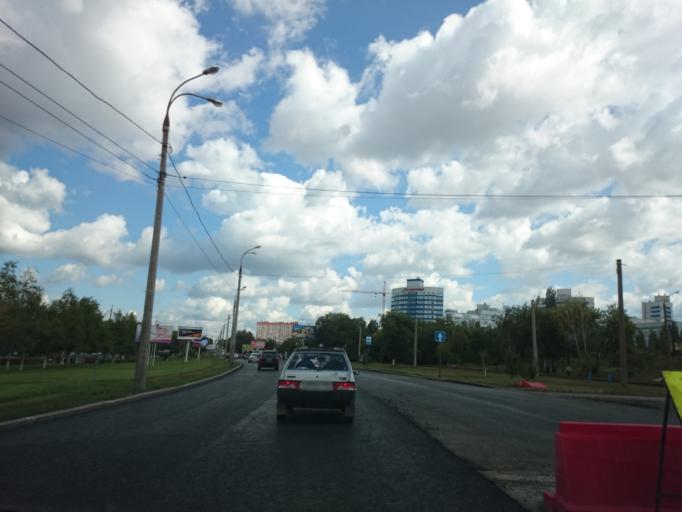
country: RU
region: Samara
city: Samara
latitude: 53.2228
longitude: 50.1686
